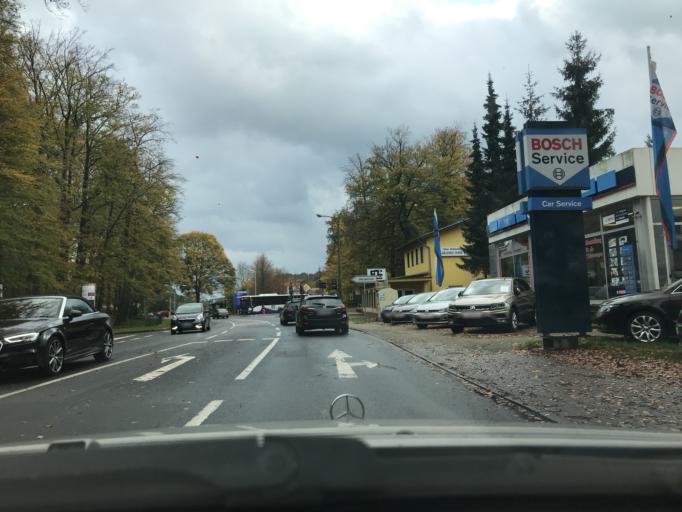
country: DE
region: Mecklenburg-Vorpommern
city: Seebad Heringsdorf
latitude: 53.9512
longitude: 14.1672
